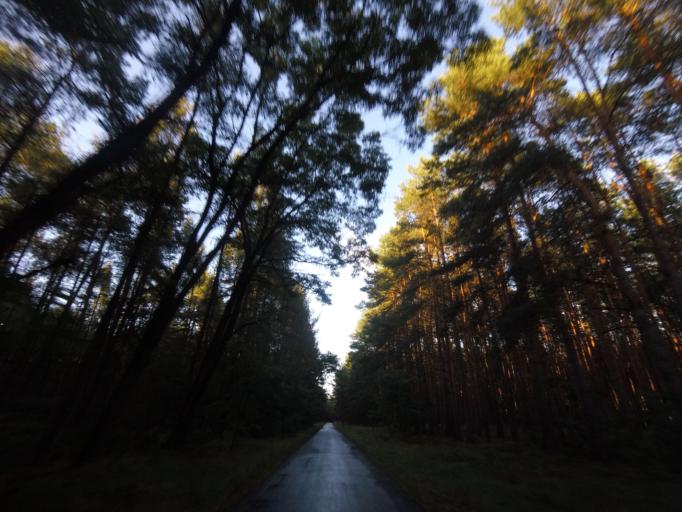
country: DE
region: Brandenburg
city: Treuenbrietzen
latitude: 52.0328
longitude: 12.8571
